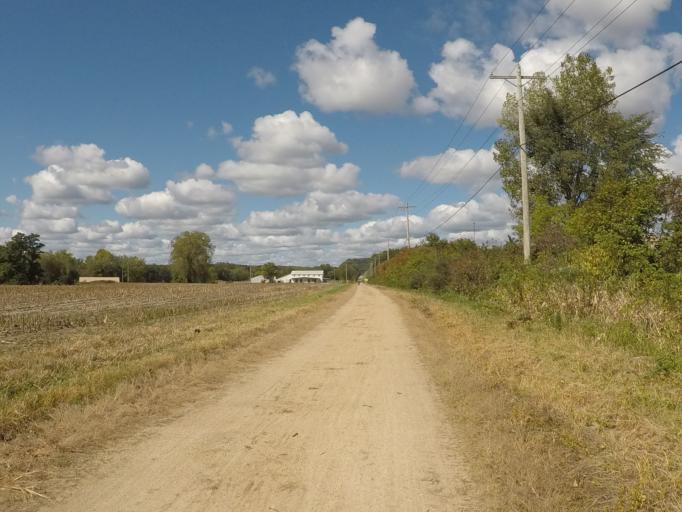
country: US
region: Wisconsin
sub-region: Richland County
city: Richland Center
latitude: 43.3109
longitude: -90.3475
